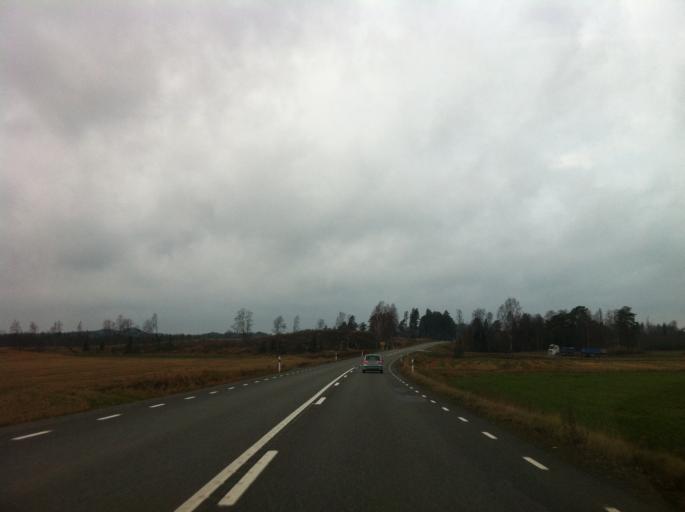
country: SE
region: Joenkoeping
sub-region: Vetlanda Kommun
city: Landsbro
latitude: 57.4025
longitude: 14.9335
